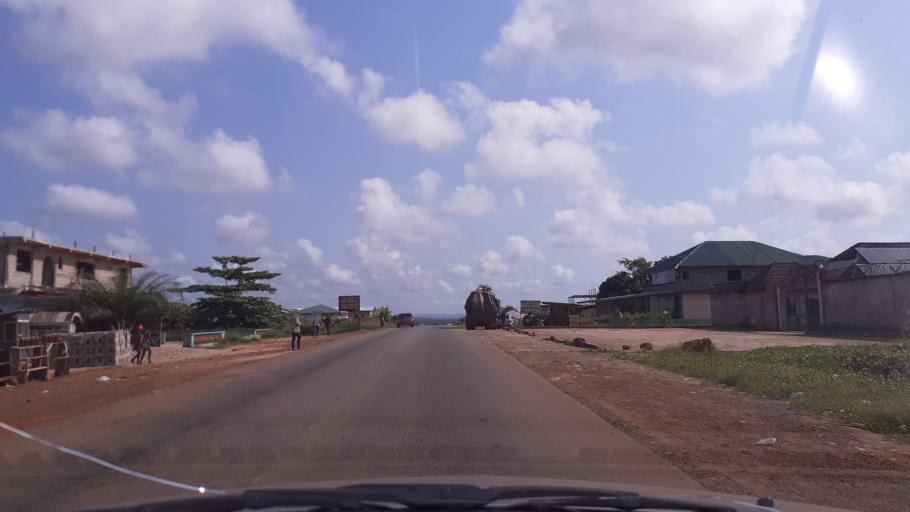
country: LR
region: Montserrado
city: Bensonville City
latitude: 6.2253
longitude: -10.5341
